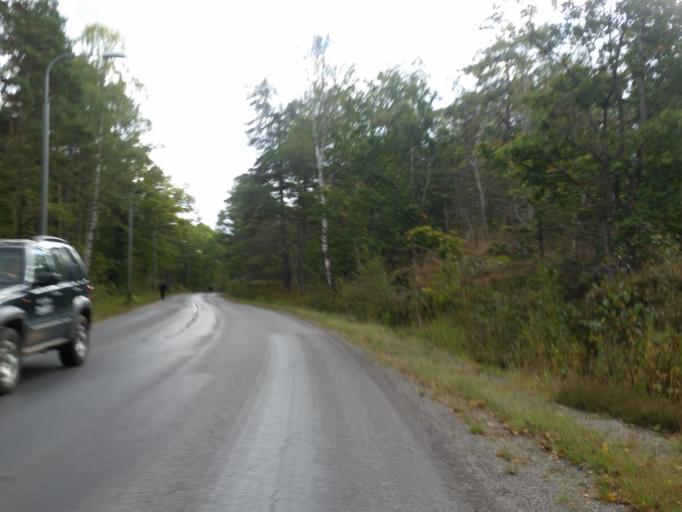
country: SE
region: Stockholm
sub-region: Nacka Kommun
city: Alta
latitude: 59.2556
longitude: 18.1357
